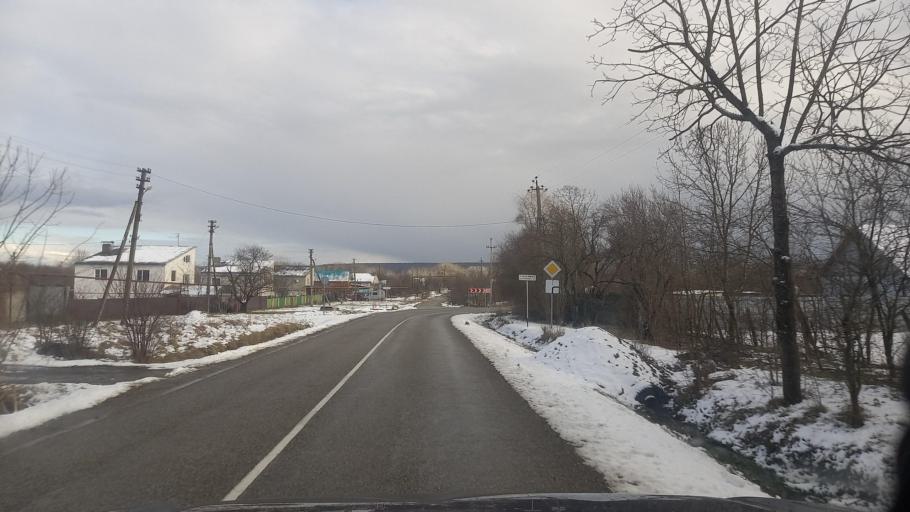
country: RU
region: Krasnodarskiy
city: Smolenskaya
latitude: 44.7764
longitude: 38.8449
